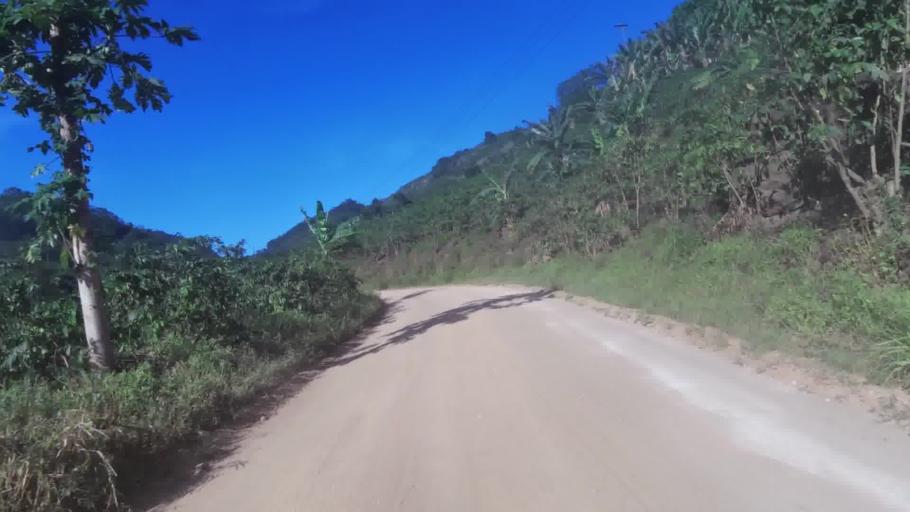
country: BR
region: Espirito Santo
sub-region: Iconha
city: Iconha
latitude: -20.7616
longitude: -40.8262
